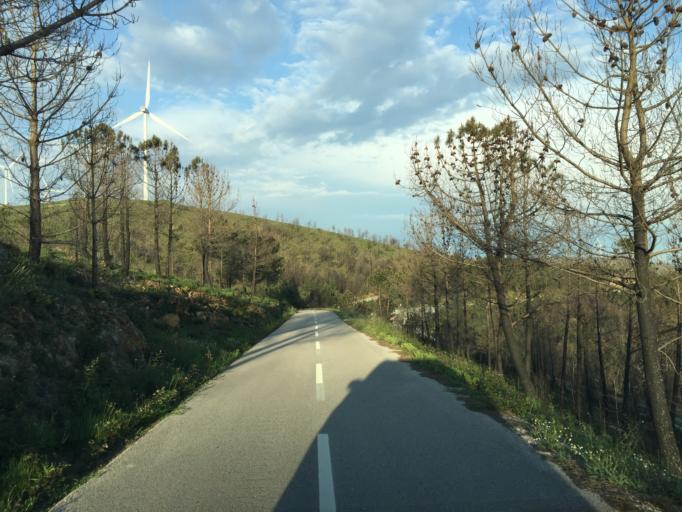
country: PT
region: Coimbra
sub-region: Pampilhosa da Serra
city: Pampilhosa da Serra
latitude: 40.1111
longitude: -8.0186
